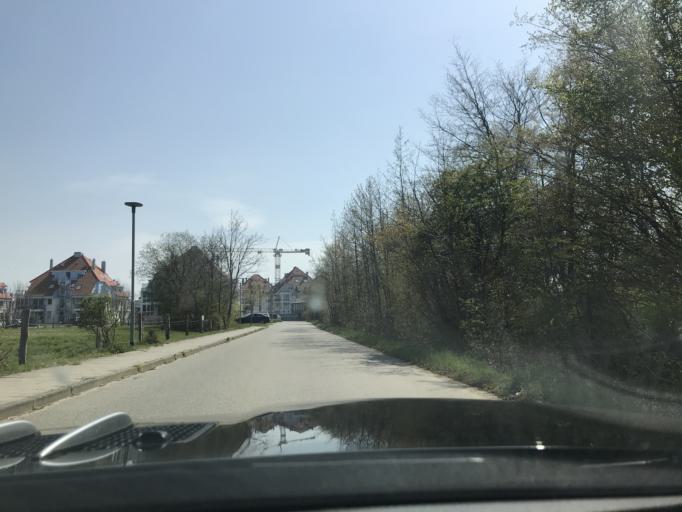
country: DE
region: Schleswig-Holstein
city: Grossenbrode
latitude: 54.3628
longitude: 11.0908
